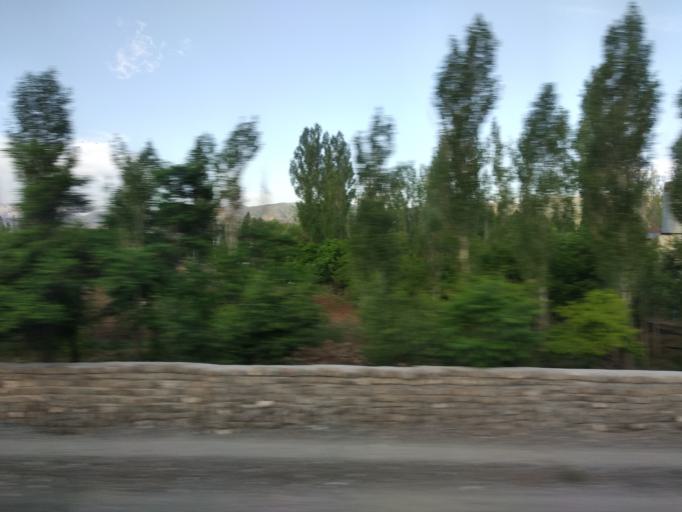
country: TR
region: Erzincan
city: Catalarmut
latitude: 39.8081
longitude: 39.3635
